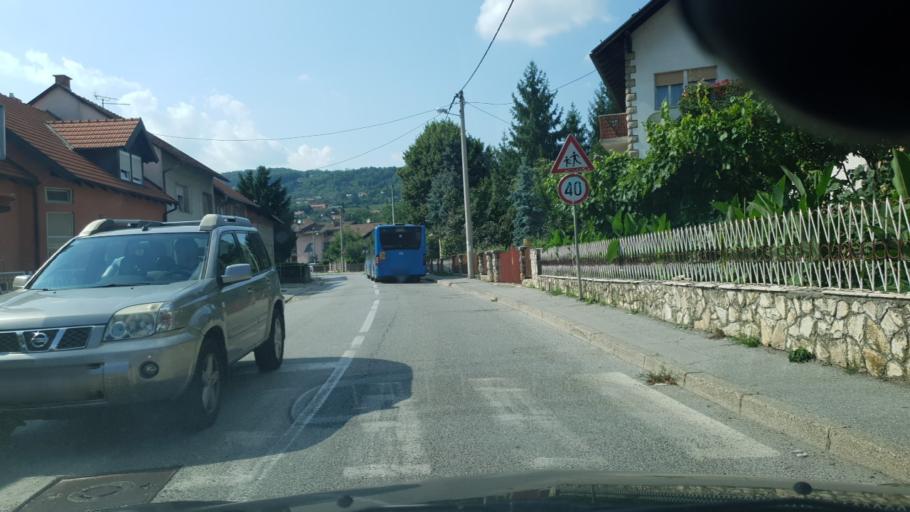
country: HR
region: Grad Zagreb
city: Stenjevec
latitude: 45.8310
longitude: 15.9048
